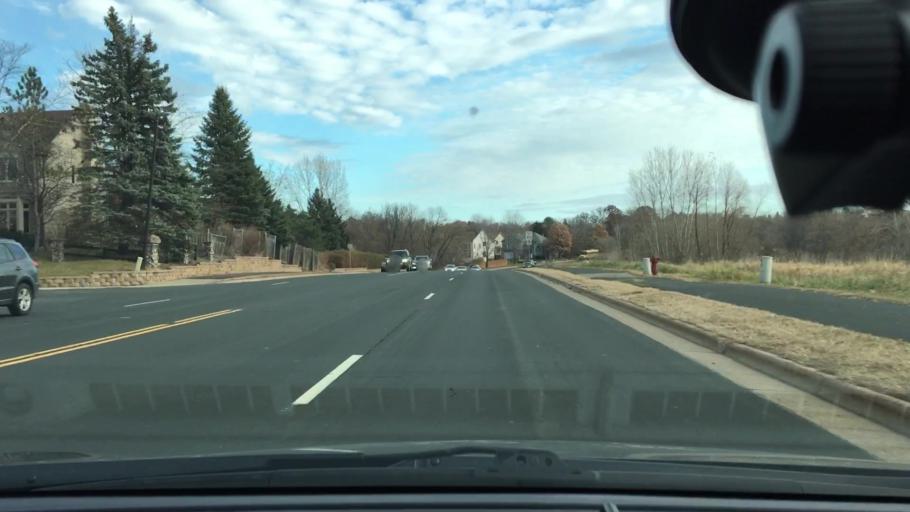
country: US
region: Minnesota
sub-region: Hennepin County
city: Maple Grove
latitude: 45.1072
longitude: -93.4812
